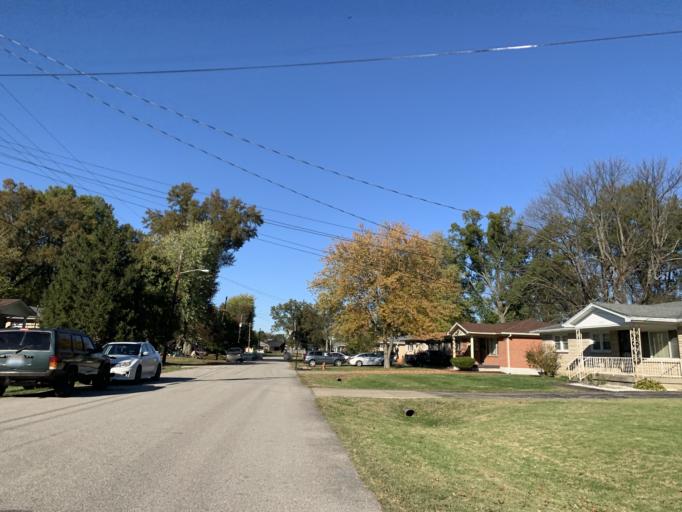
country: US
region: Kentucky
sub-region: Jefferson County
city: Pleasure Ridge Park
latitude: 38.1611
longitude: -85.8644
